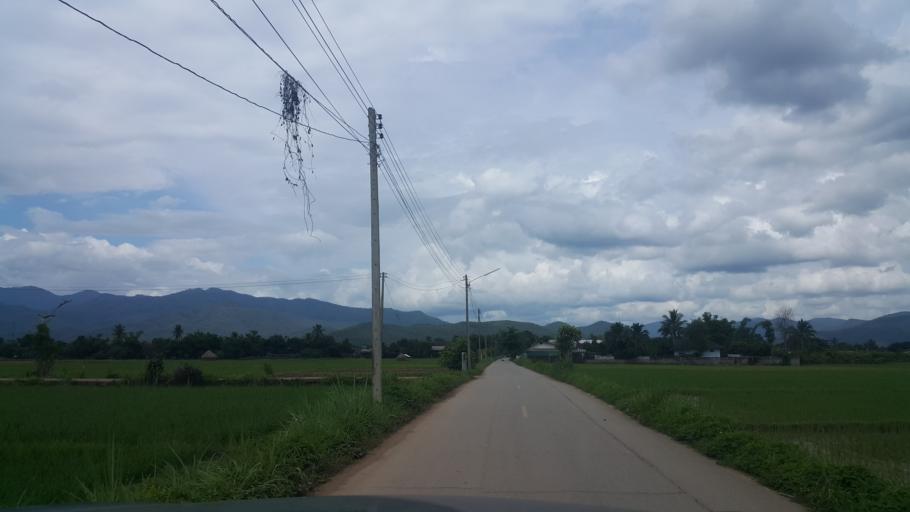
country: TH
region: Chiang Mai
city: Mae Taeng
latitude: 19.1815
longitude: 98.9858
